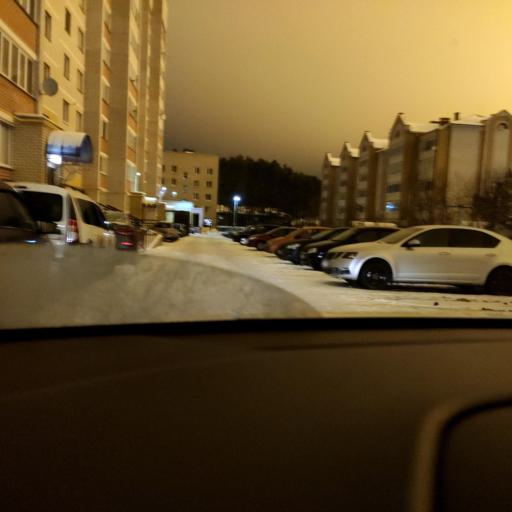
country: RU
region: Tatarstan
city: Osinovo
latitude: 55.8756
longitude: 48.8975
